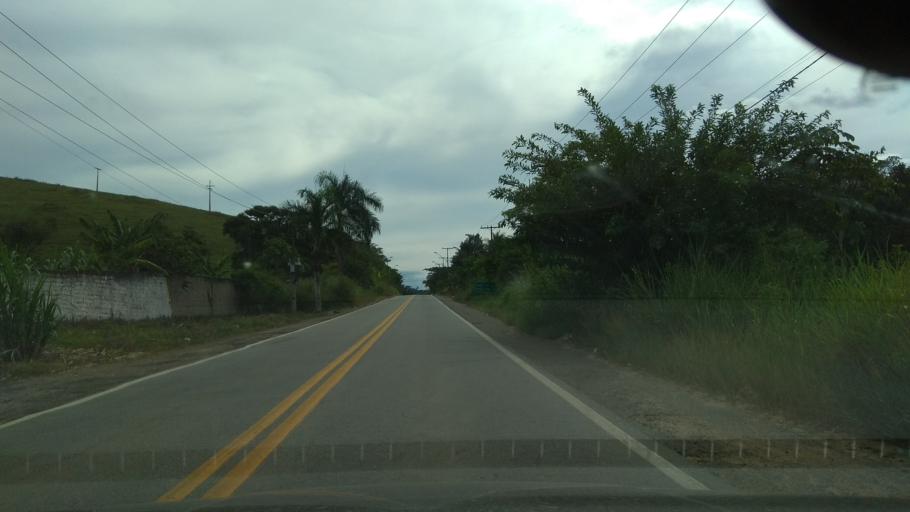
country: BR
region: Bahia
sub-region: Ubata
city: Ubata
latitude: -14.1968
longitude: -39.5420
